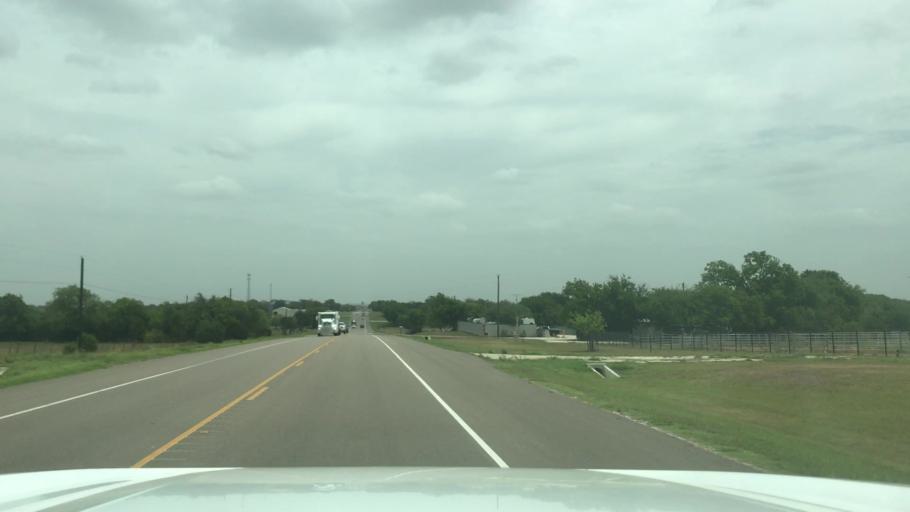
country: US
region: Texas
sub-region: McLennan County
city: Woodway
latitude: 31.5877
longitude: -97.3225
